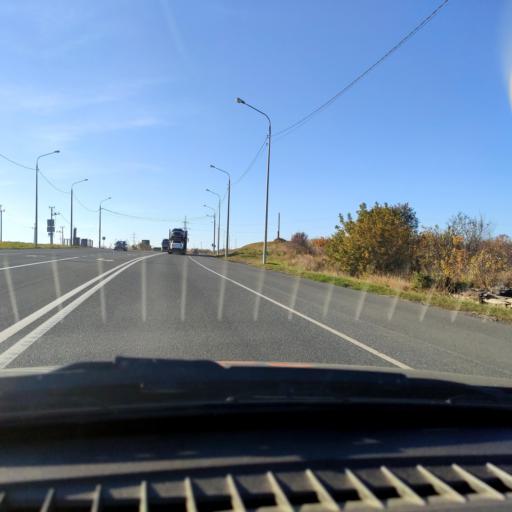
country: RU
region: Samara
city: Mezhdurechensk
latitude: 53.2486
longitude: 49.1679
